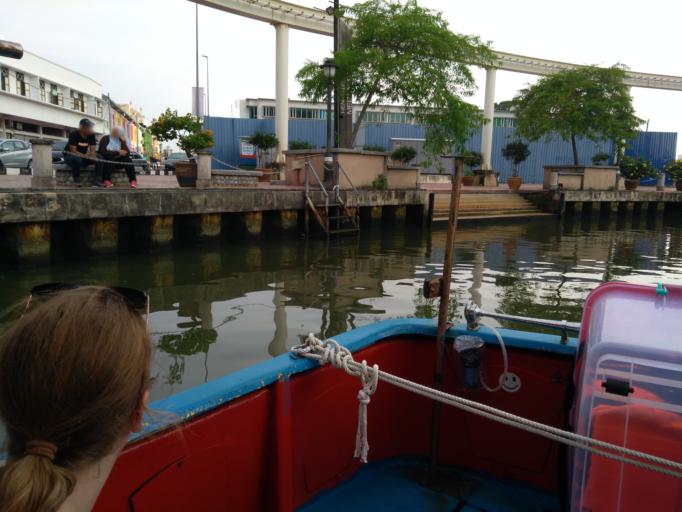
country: MY
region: Melaka
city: Malacca
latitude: 2.2022
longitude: 102.2516
